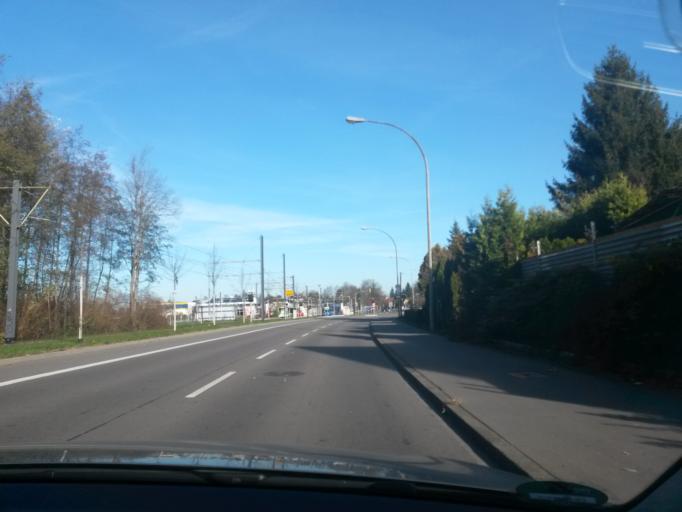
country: DE
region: Baden-Wuerttemberg
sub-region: Freiburg Region
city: Gundelfingen
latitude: 48.0335
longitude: 7.8631
